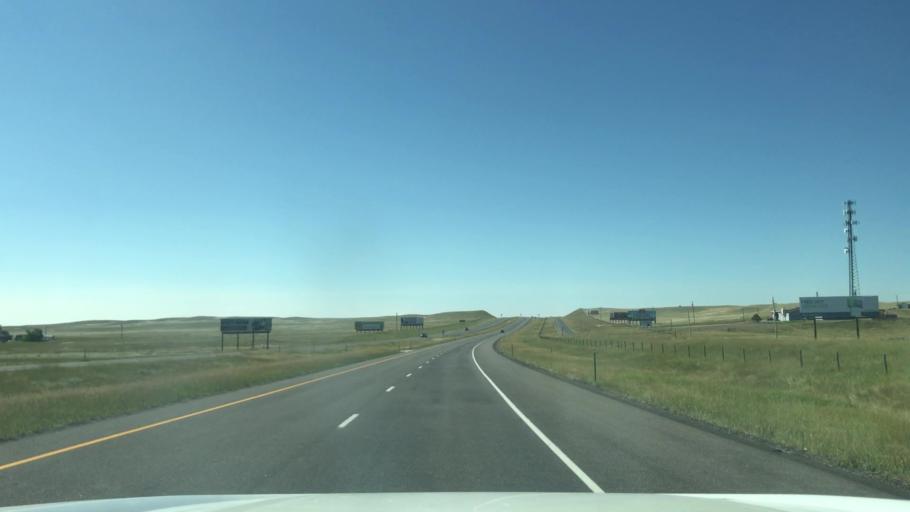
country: US
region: Wyoming
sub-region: Laramie County
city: Ranchettes
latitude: 41.2514
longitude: -104.8385
